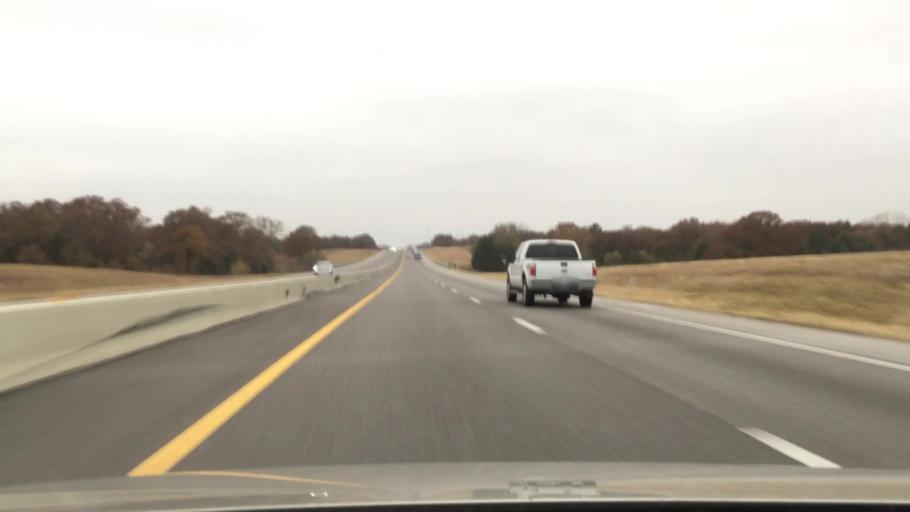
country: US
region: Oklahoma
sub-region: Lincoln County
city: Chandler
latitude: 35.7272
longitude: -96.8413
